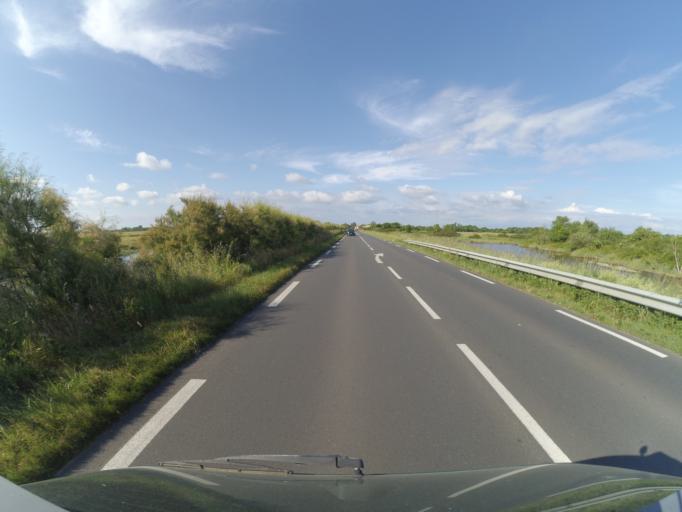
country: FR
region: Poitou-Charentes
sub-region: Departement de la Charente-Maritime
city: Le Gua
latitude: 45.7208
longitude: -0.9671
